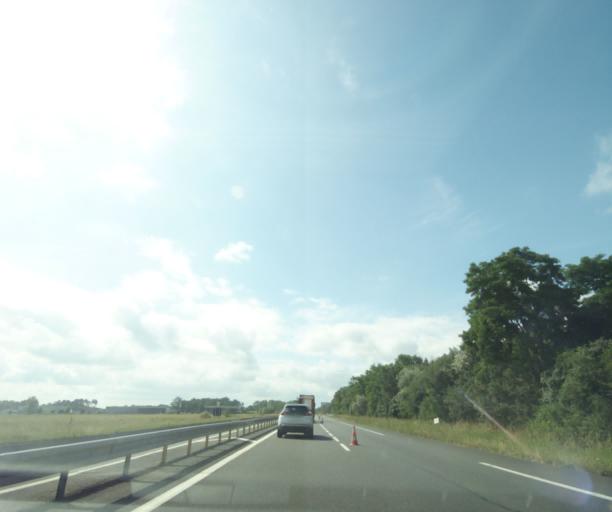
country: FR
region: Pays de la Loire
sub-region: Departement de Maine-et-Loire
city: Jumelles
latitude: 47.4101
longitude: -0.1232
